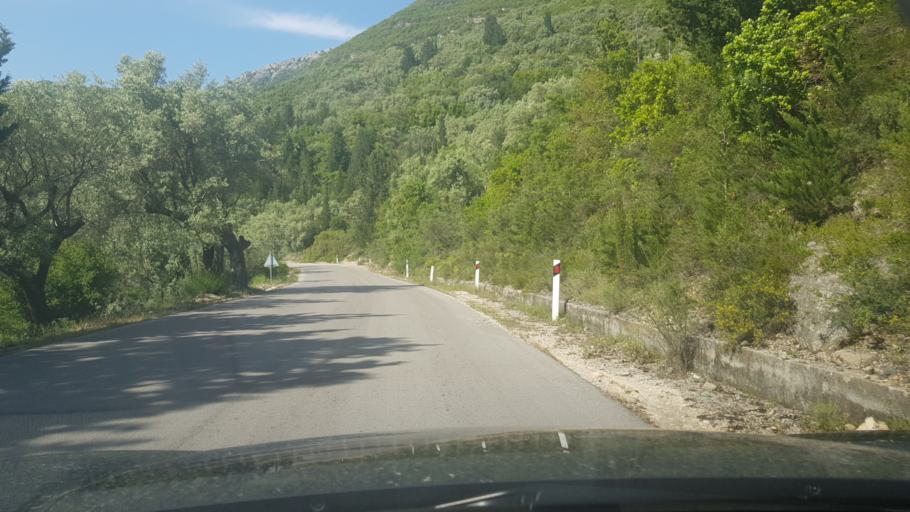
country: GR
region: Ionian Islands
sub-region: Lefkada
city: Nidri
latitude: 38.6566
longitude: 20.6568
